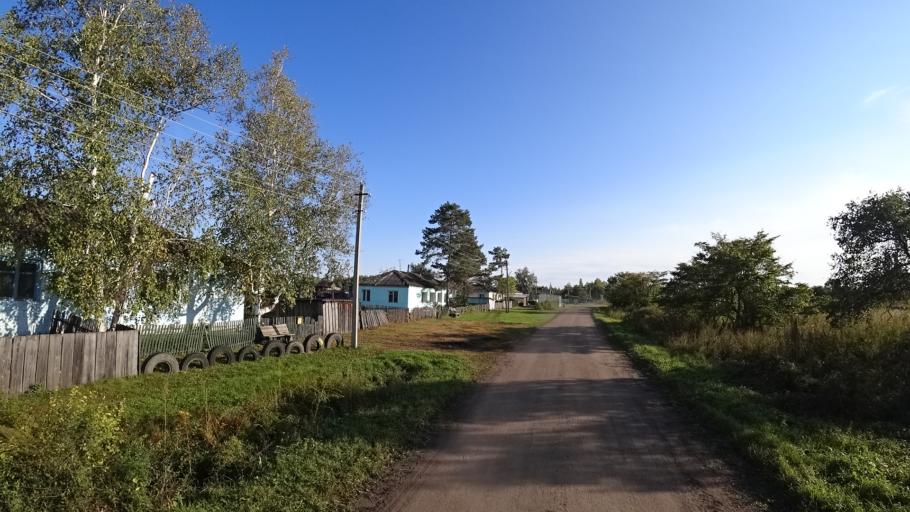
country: RU
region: Amur
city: Arkhara
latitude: 49.3566
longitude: 130.1228
